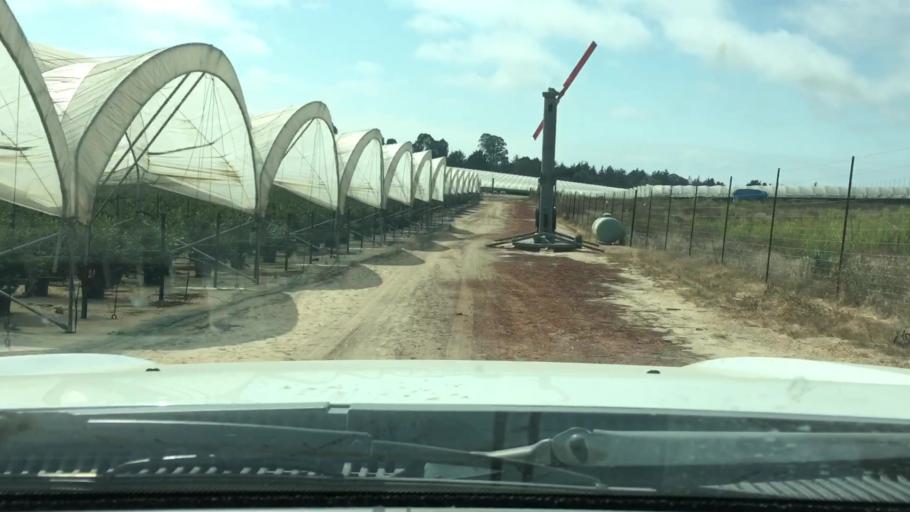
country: US
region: California
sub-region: San Luis Obispo County
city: Callender
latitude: 35.0645
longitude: -120.5654
